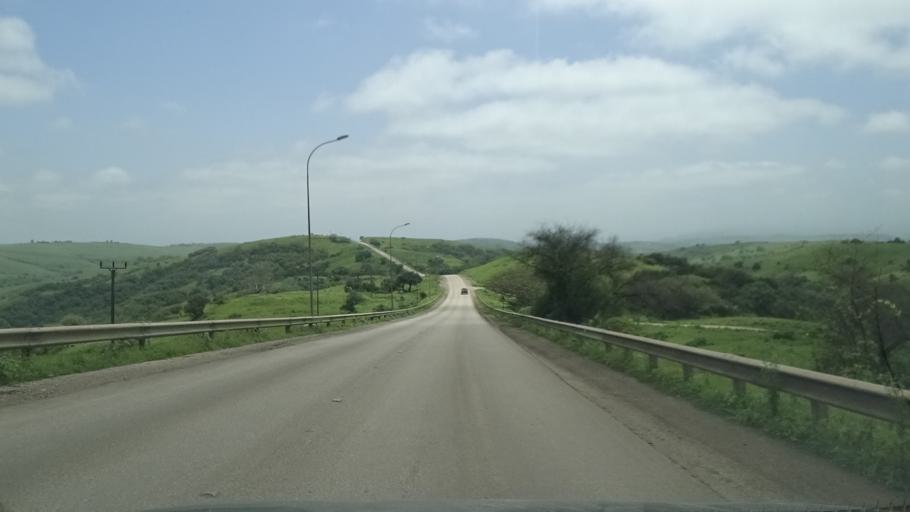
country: OM
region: Zufar
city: Salalah
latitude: 17.2081
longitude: 54.2452
